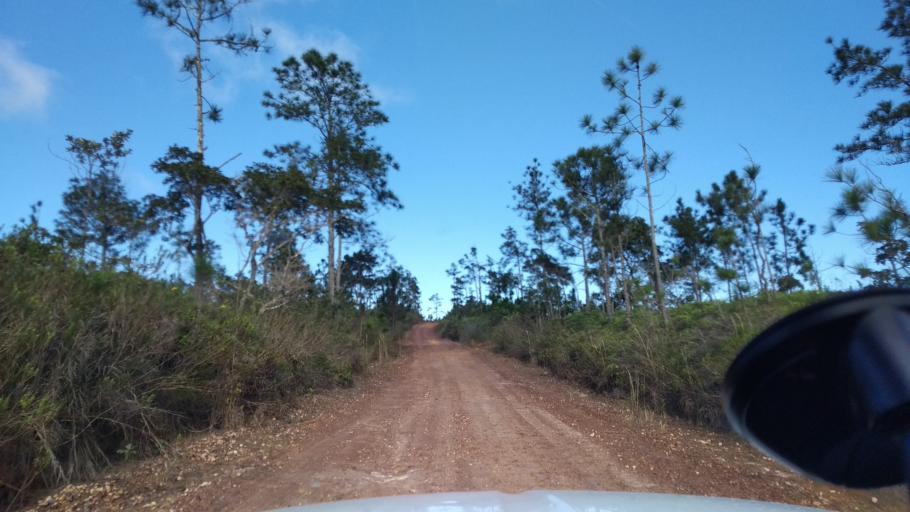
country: BZ
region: Cayo
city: Belmopan
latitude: 16.9971
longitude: -88.8381
